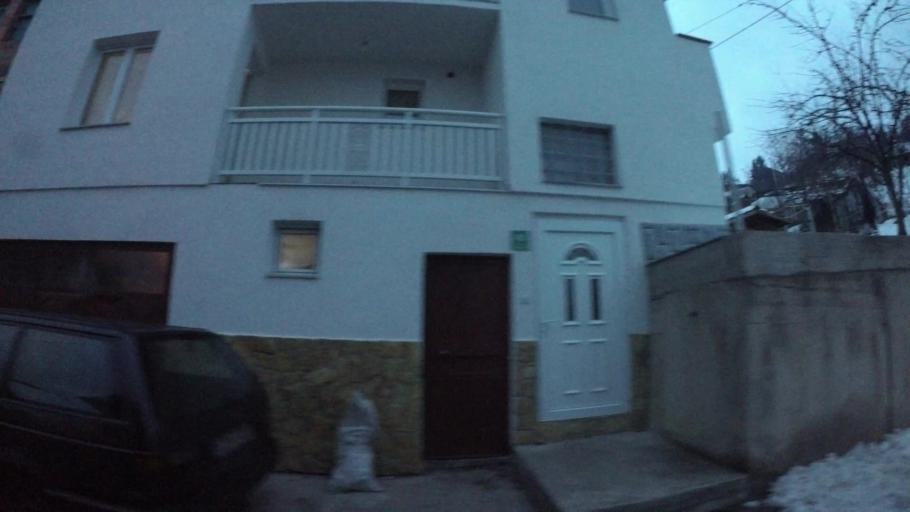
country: BA
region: Federation of Bosnia and Herzegovina
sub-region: Kanton Sarajevo
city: Sarajevo
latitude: 43.8563
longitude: 18.3364
